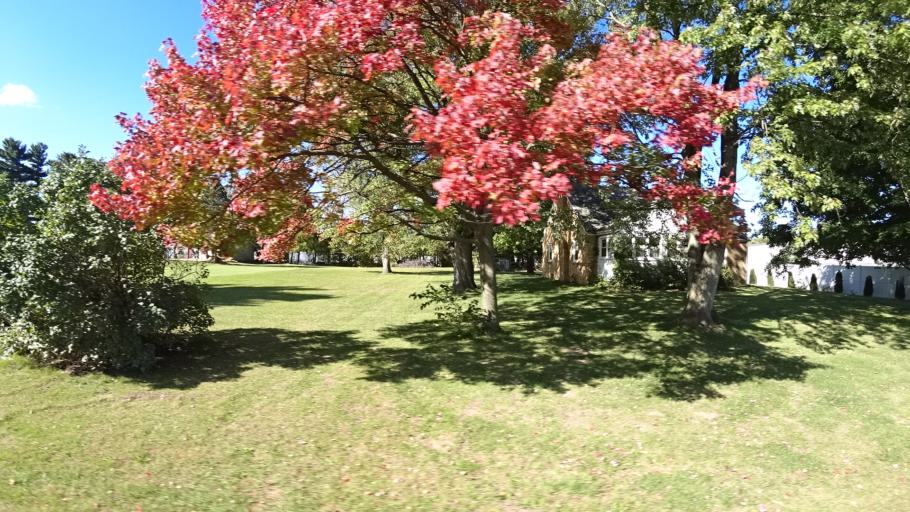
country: US
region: Indiana
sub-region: LaPorte County
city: Michigan City
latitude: 41.6794
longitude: -86.9133
